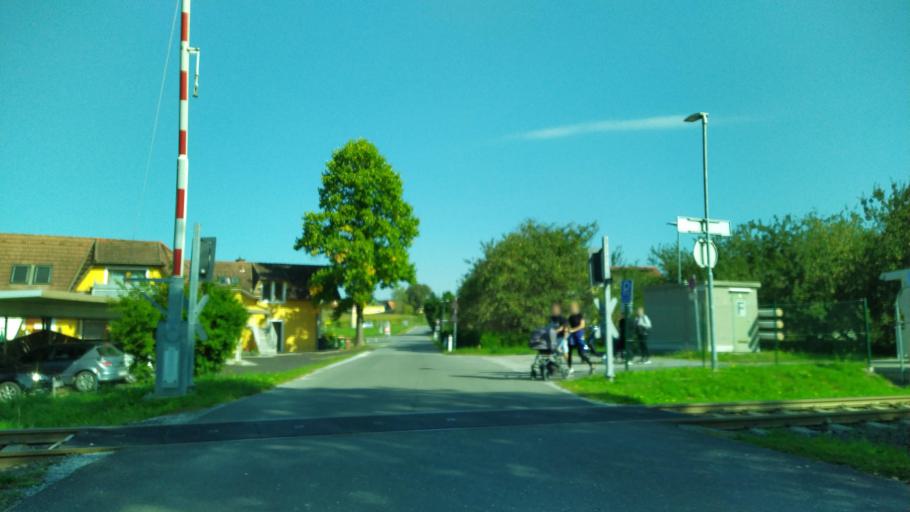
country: AT
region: Styria
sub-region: Politischer Bezirk Deutschlandsberg
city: Gross Sankt Florian
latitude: 46.8296
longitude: 15.3476
